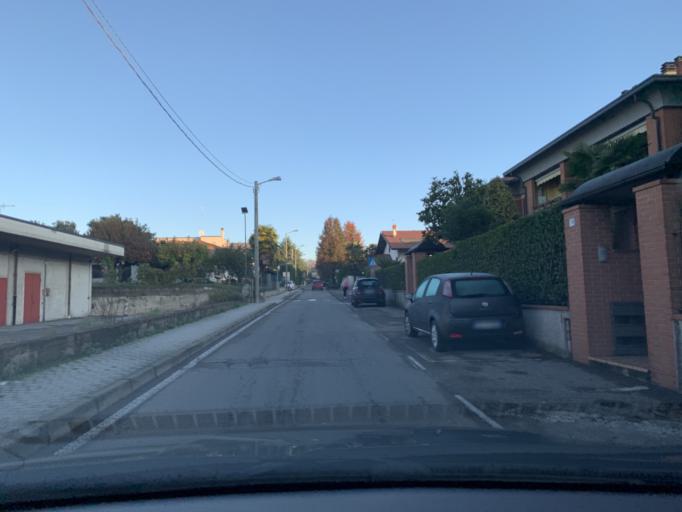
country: IT
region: Lombardy
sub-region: Provincia di Como
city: Bregnano
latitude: 45.6967
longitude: 9.0645
